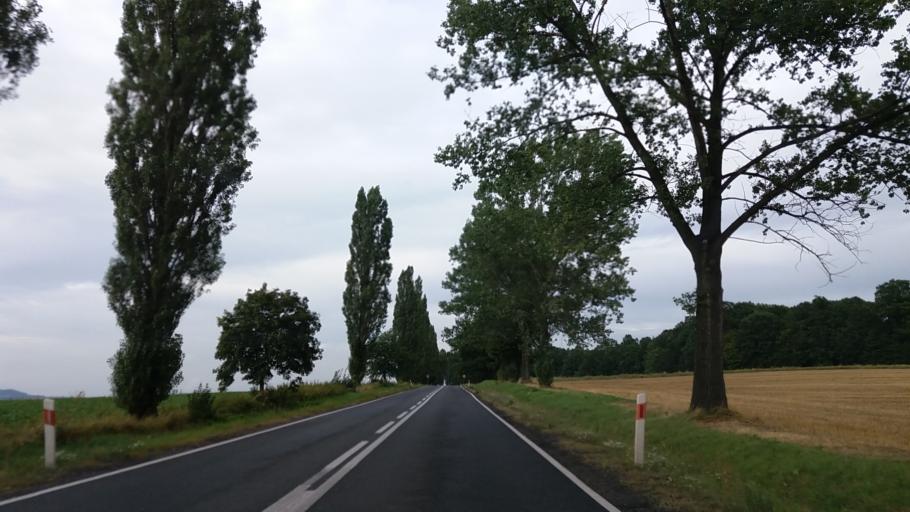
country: PL
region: Lower Silesian Voivodeship
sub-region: Powiat swidnicki
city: Swiebodzice
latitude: 50.8903
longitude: 16.3436
